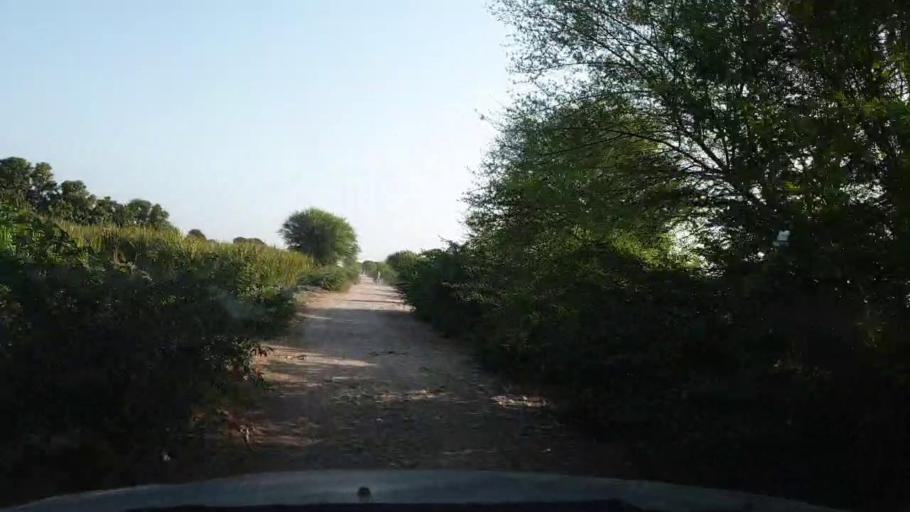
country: PK
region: Sindh
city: Tando Ghulam Ali
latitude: 25.1271
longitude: 68.9407
